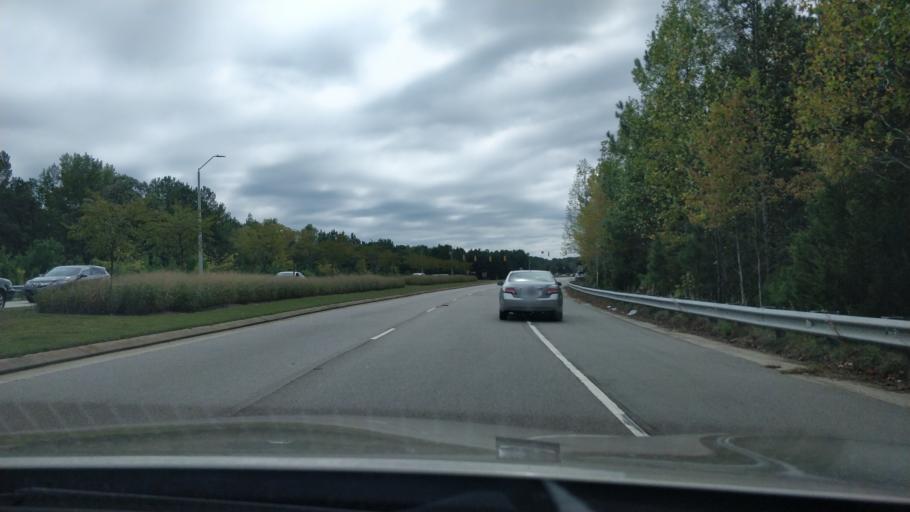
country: US
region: North Carolina
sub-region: Wake County
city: Morrisville
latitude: 35.9140
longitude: -78.7287
